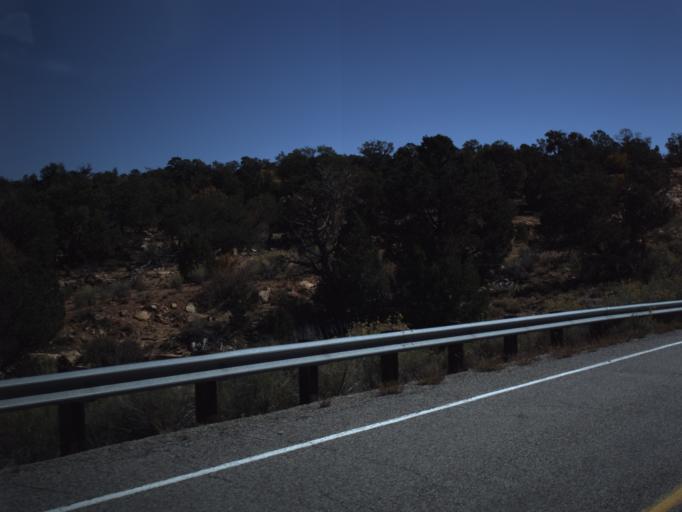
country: US
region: Utah
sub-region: San Juan County
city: Blanding
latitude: 37.5858
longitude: -109.8952
